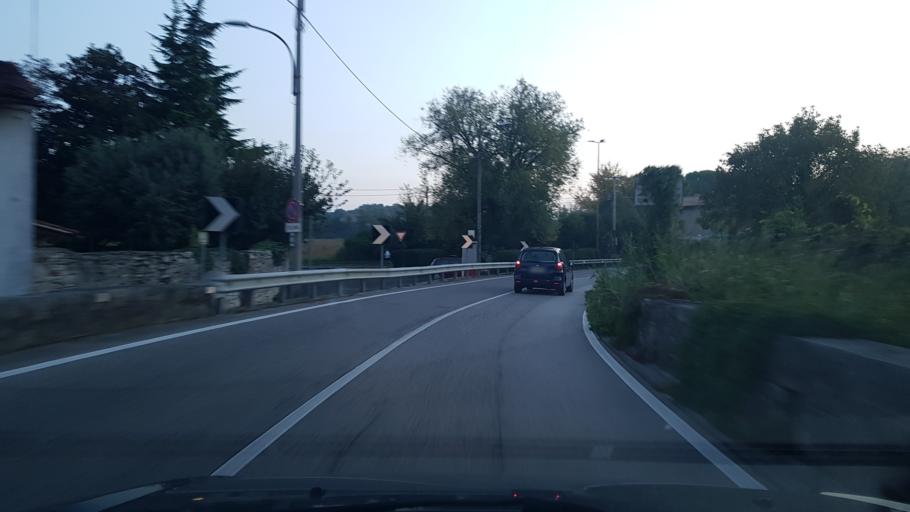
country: IT
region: Friuli Venezia Giulia
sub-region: Provincia di Gorizia
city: Ronchi dei Legionari
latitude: 45.8252
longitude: 13.5229
